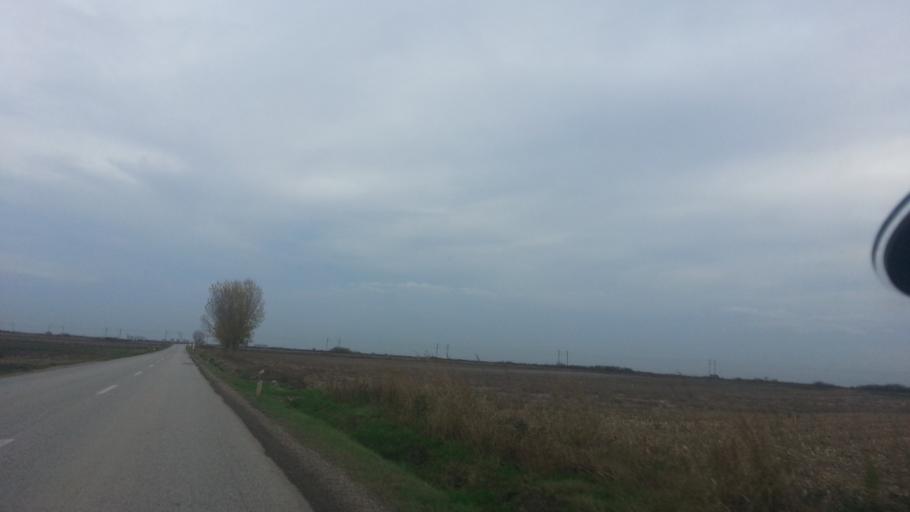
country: RS
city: Putinci
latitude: 44.9910
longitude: 19.9902
